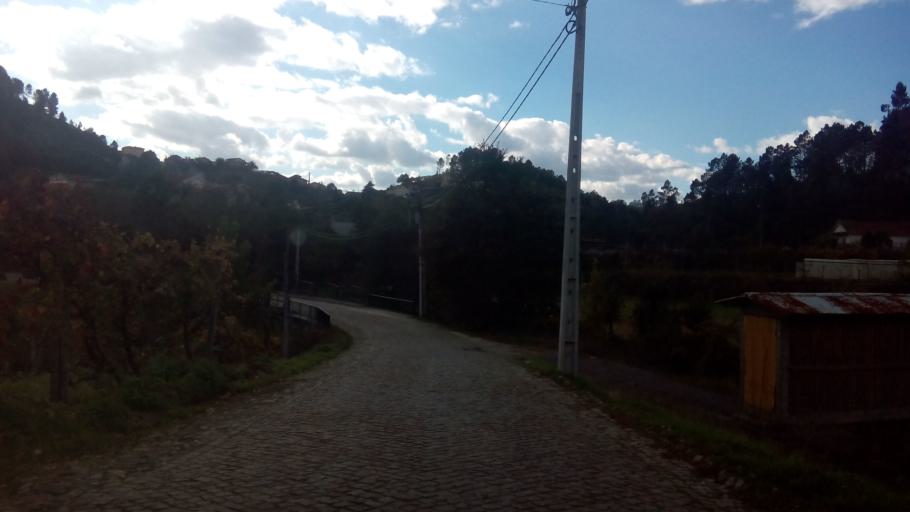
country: PT
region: Porto
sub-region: Amarante
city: Amarante
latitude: 41.2681
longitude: -8.0061
